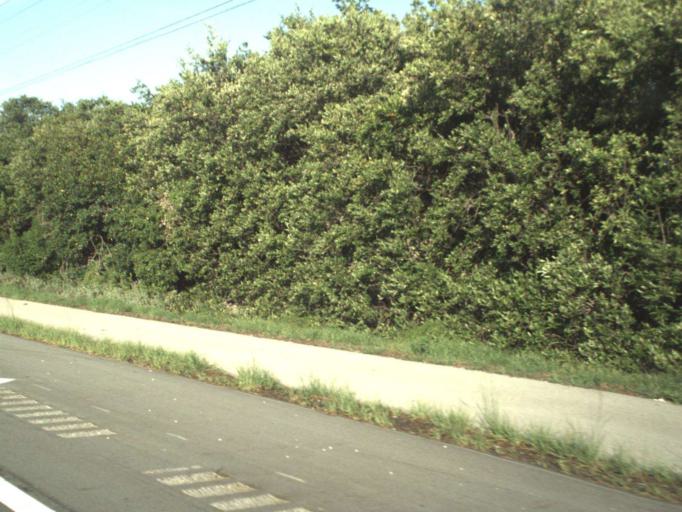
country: US
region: Florida
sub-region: Monroe County
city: Islamorada
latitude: 24.8292
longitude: -80.8095
